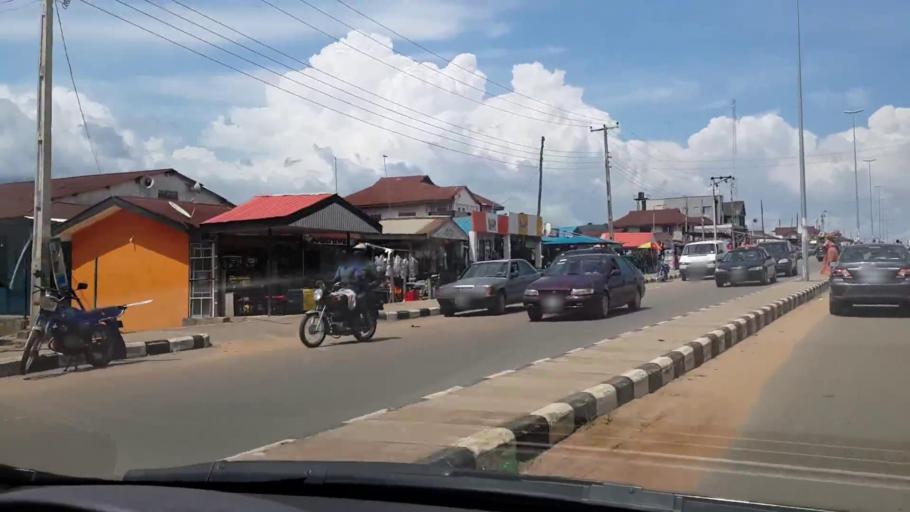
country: NG
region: Ondo
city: Ondo
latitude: 7.0996
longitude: 4.8426
